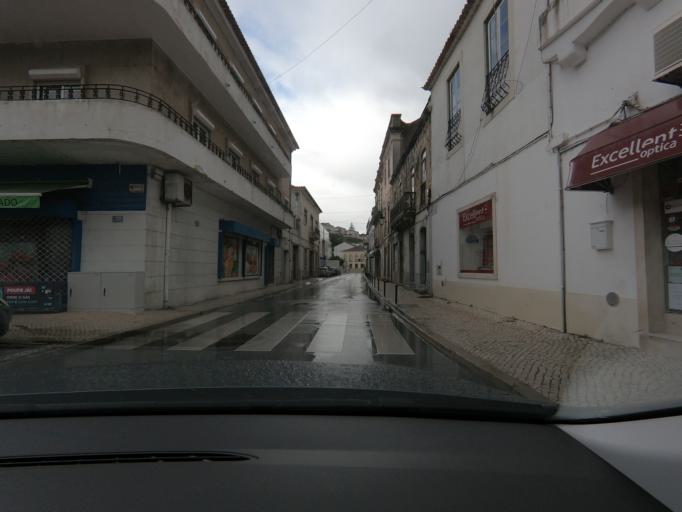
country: PT
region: Lisbon
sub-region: Alenquer
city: Alenquer
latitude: 39.0526
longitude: -9.0083
